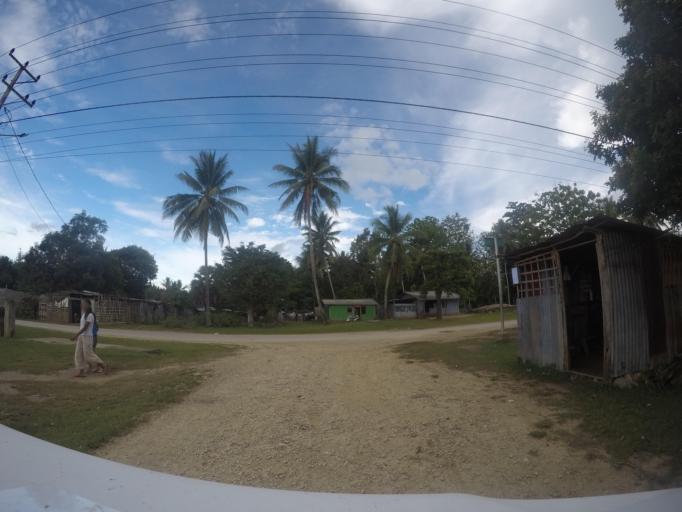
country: TL
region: Lautem
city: Lospalos
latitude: -8.5090
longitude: 126.9870
